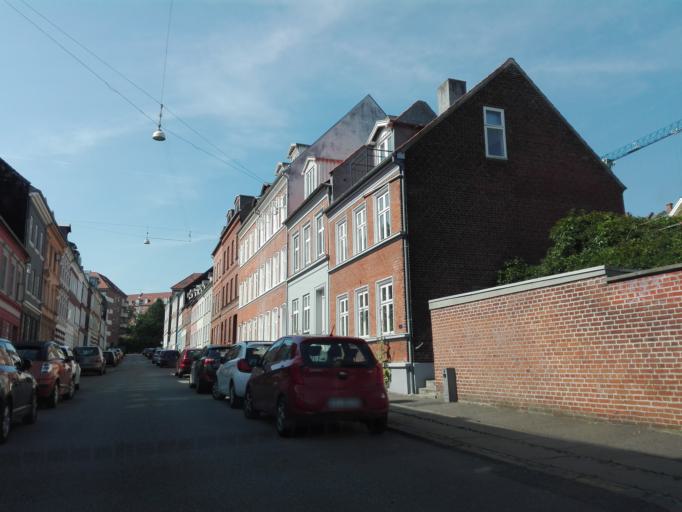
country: DK
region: Central Jutland
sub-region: Arhus Kommune
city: Arhus
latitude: 56.1635
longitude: 10.2042
